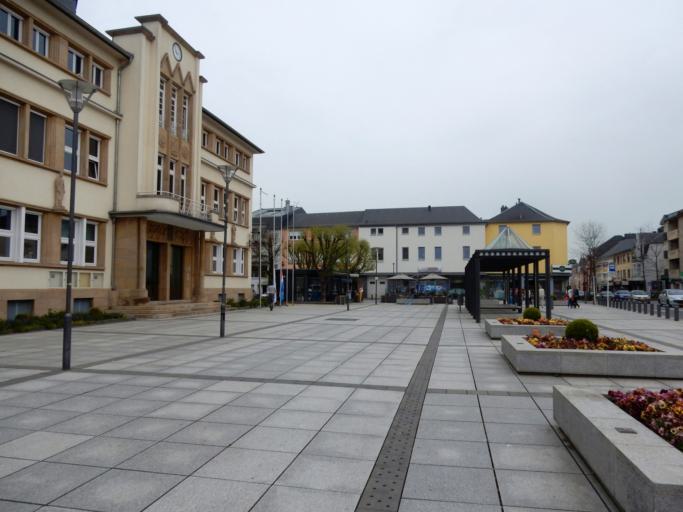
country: LU
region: Luxembourg
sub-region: Canton d'Esch-sur-Alzette
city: Petange
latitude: 49.5565
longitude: 5.8773
